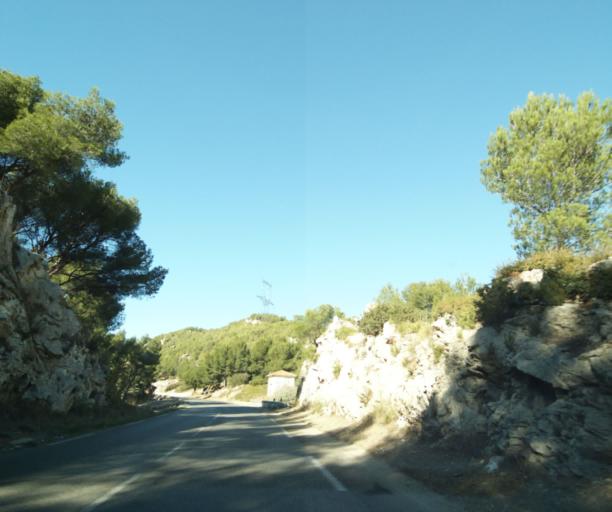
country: FR
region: Provence-Alpes-Cote d'Azur
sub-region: Departement des Bouches-du-Rhone
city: Le Rove
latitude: 43.3626
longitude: 5.2703
